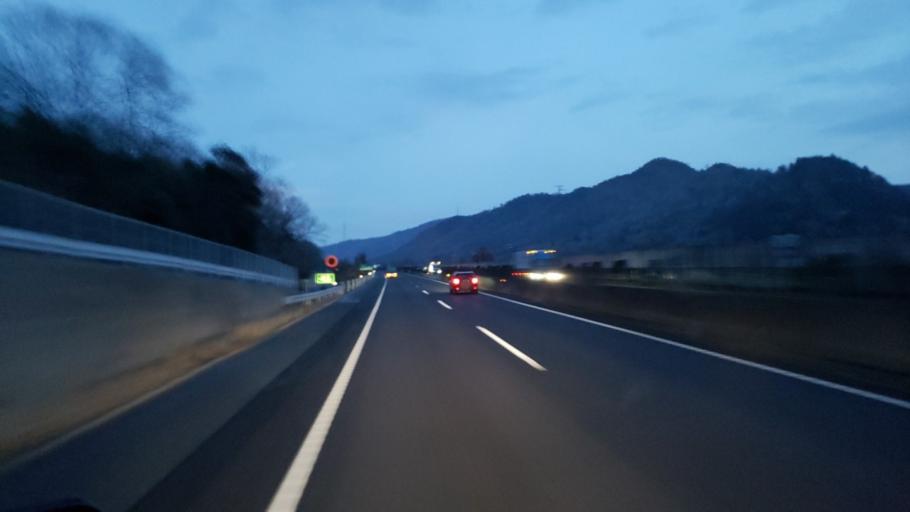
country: JP
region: Hyogo
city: Kakogawacho-honmachi
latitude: 34.8517
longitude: 134.7903
